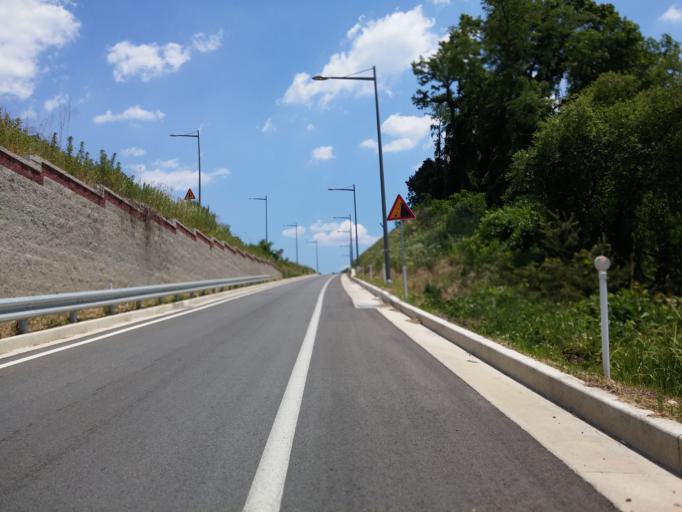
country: KR
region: Chungcheongbuk-do
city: Cheongju-si
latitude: 36.6020
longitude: 127.4419
